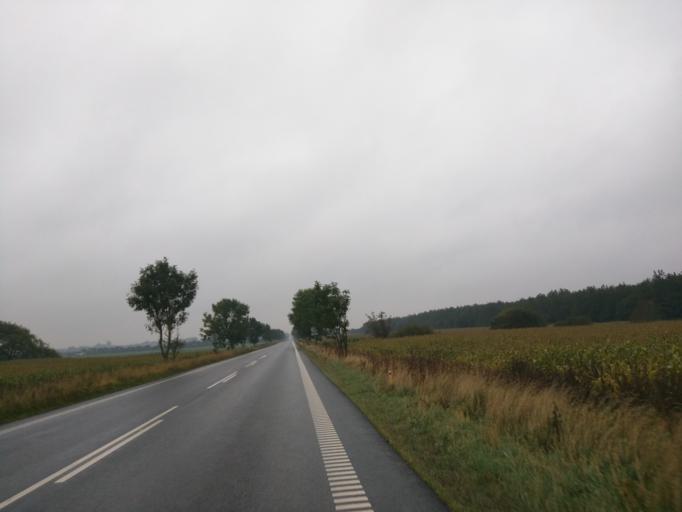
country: DK
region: Central Jutland
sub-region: Viborg Kommune
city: Viborg
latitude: 56.3750
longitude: 9.4410
